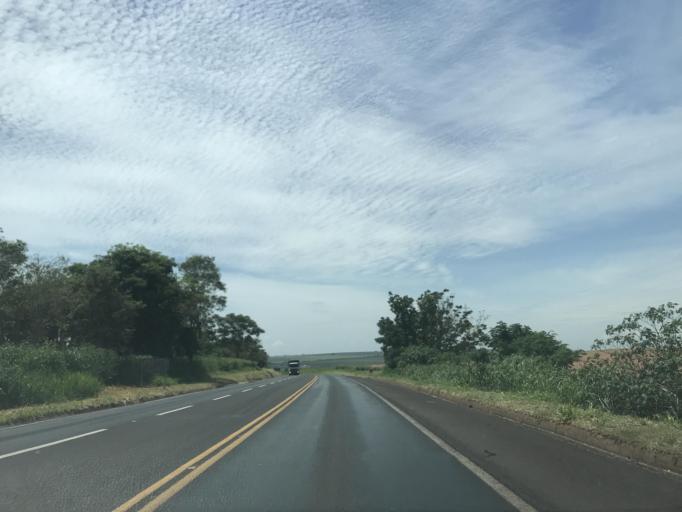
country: BR
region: Parana
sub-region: Paranavai
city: Nova Aurora
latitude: -22.9932
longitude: -52.5908
